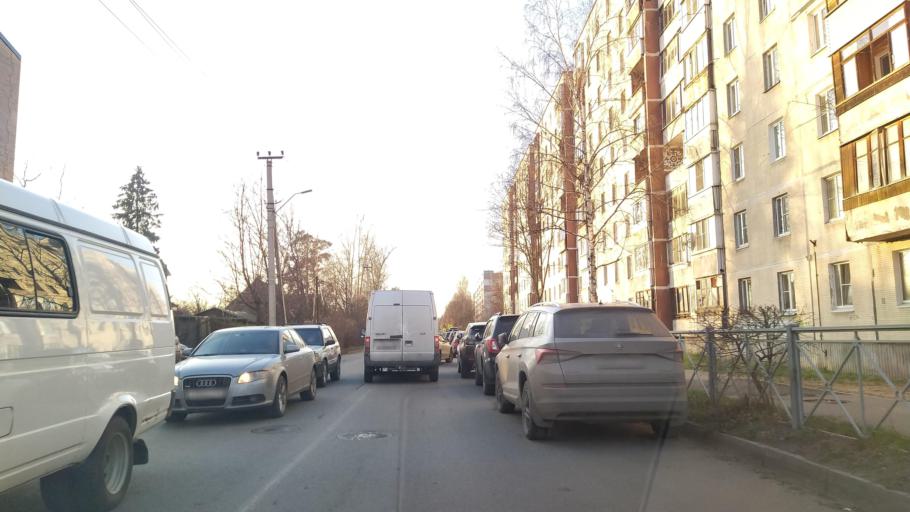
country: RU
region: Leningrad
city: Vsevolozhsk
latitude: 60.0232
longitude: 30.6314
